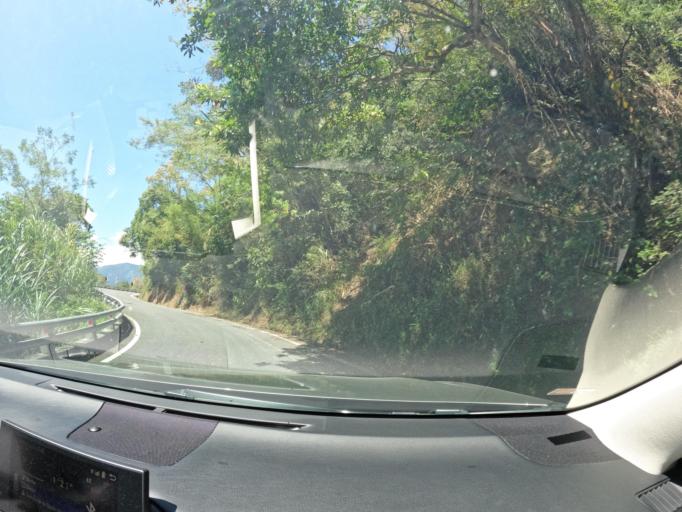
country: TW
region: Taiwan
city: Yujing
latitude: 23.2760
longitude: 120.8435
